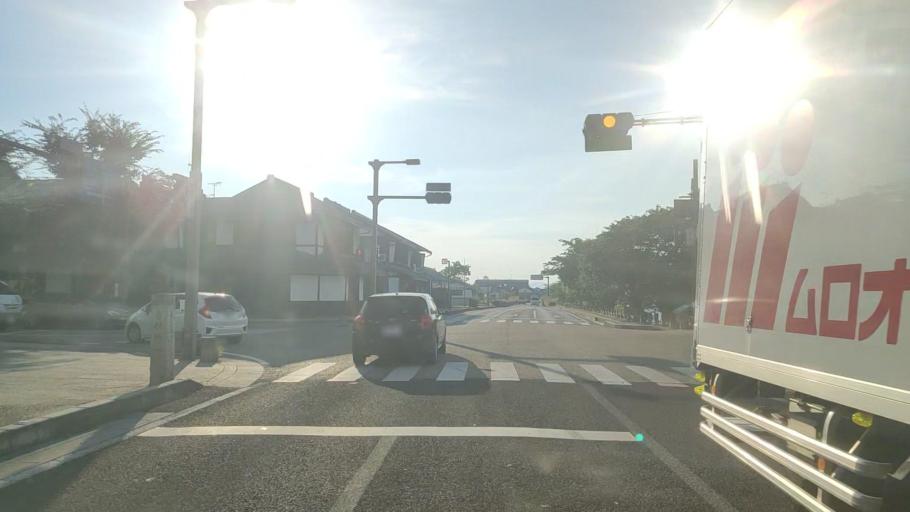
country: JP
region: Shiga Prefecture
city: Hikone
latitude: 35.2721
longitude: 136.2527
